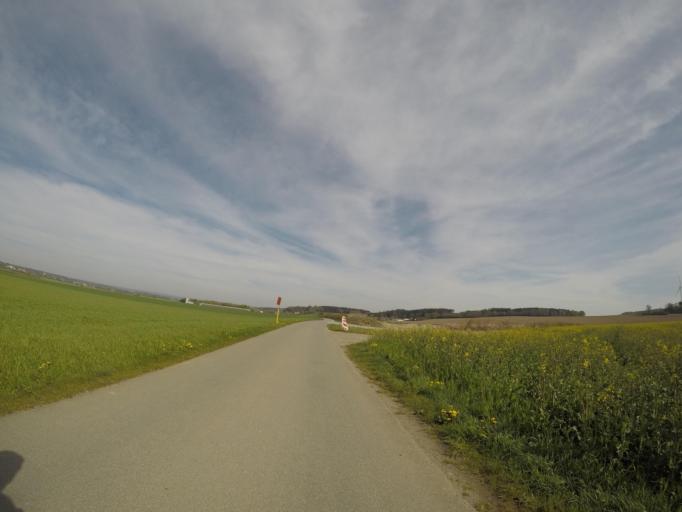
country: DE
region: Baden-Wuerttemberg
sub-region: Tuebingen Region
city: Boms
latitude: 48.0075
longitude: 9.5425
